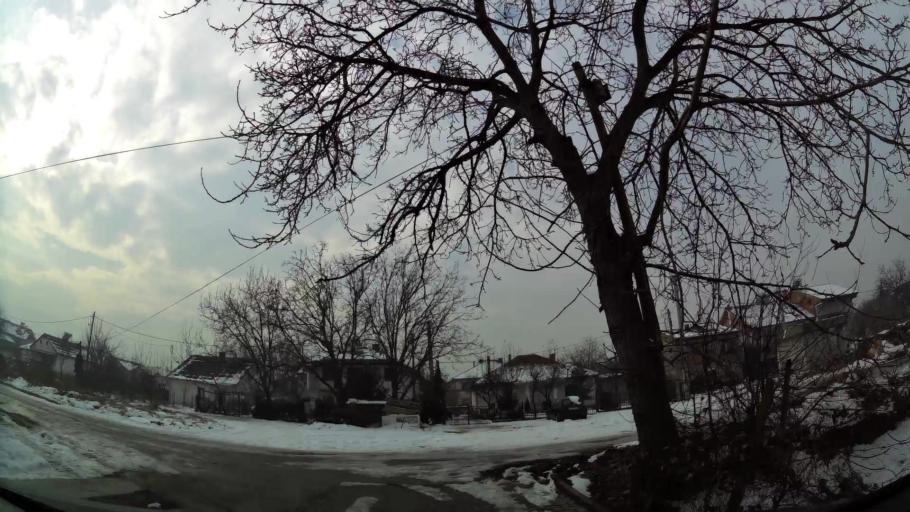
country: MK
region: Saraj
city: Saraj
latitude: 42.0248
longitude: 21.3540
